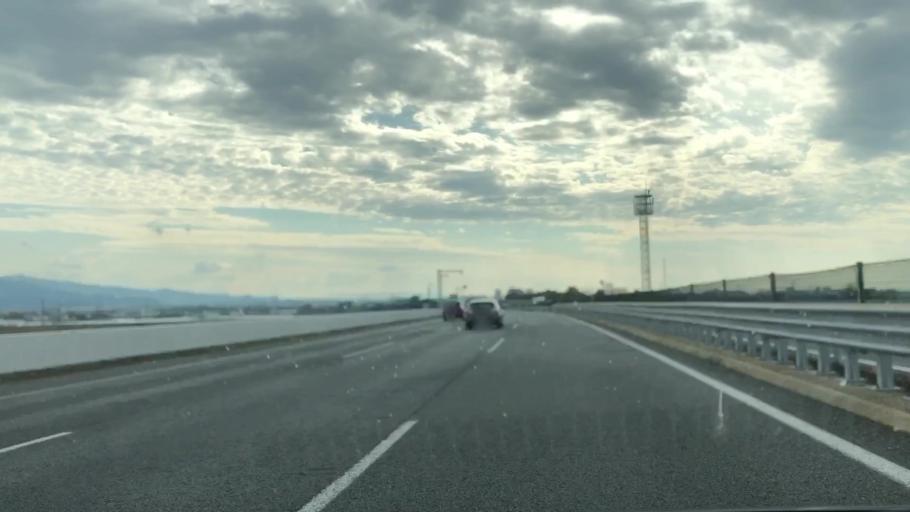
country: JP
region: Saga Prefecture
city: Tosu
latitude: 33.3538
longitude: 130.5381
